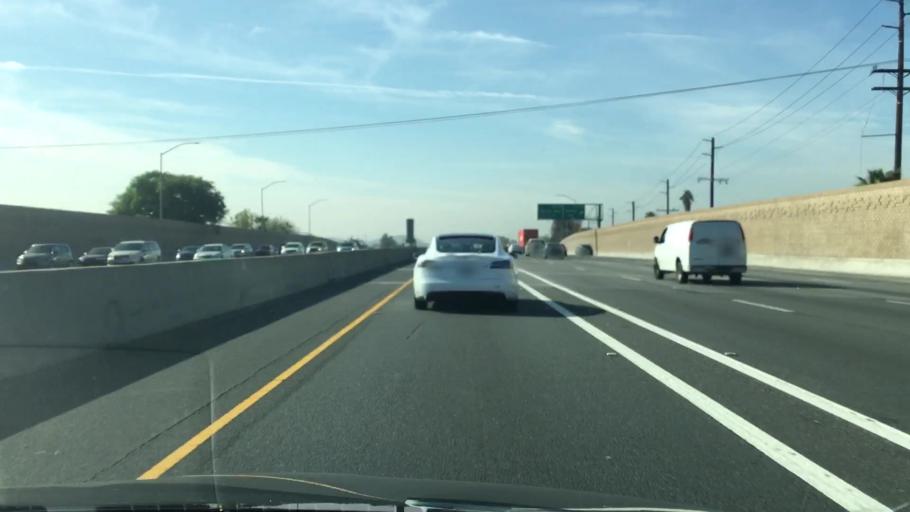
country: US
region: California
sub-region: Los Angeles County
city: Claremont
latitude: 34.0805
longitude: -117.7364
